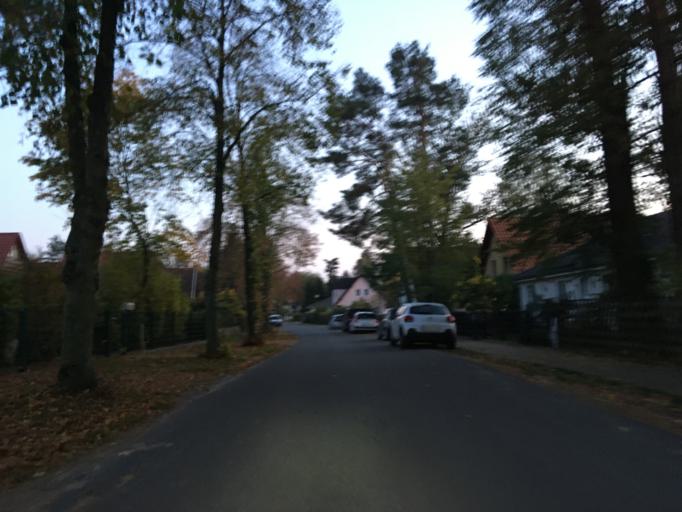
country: DE
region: Brandenburg
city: Birkenwerder
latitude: 52.6824
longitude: 13.3206
